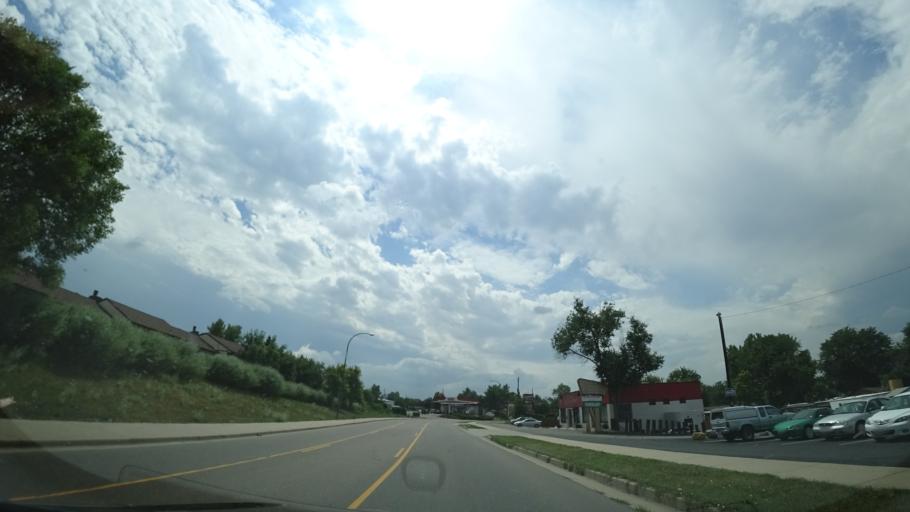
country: US
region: Colorado
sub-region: Jefferson County
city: Lakewood
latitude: 39.6965
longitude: -105.0701
